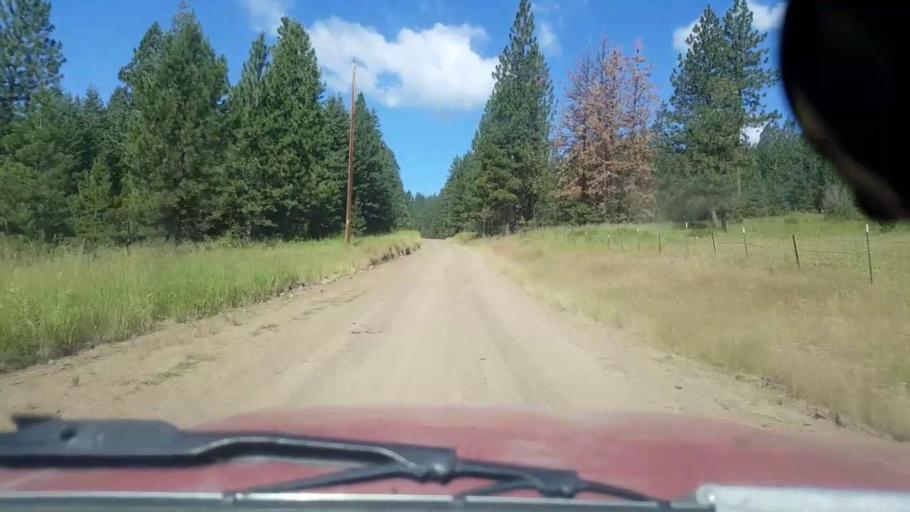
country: US
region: Washington
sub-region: Garfield County
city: Pomeroy
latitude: 46.0370
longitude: -117.4402
